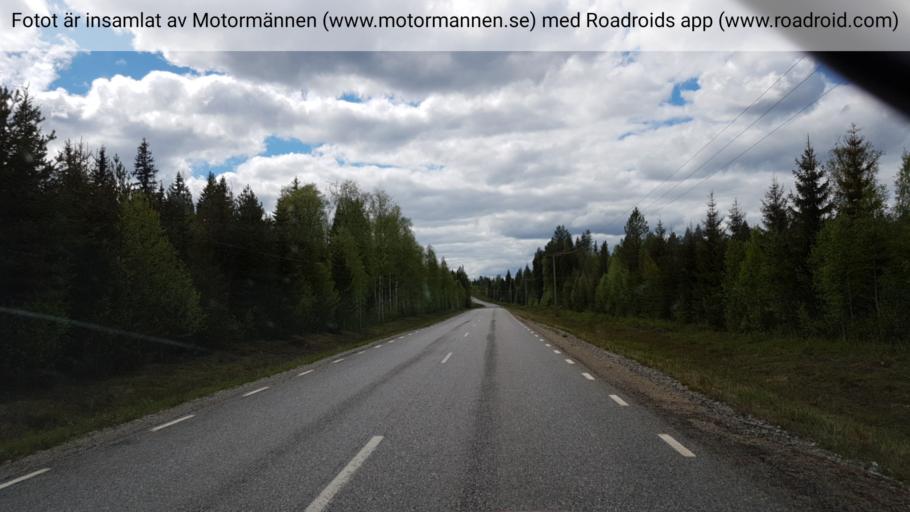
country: SE
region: Vaesterbotten
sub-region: Skelleftea Kommun
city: Langsele
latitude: 64.7708
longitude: 20.0072
